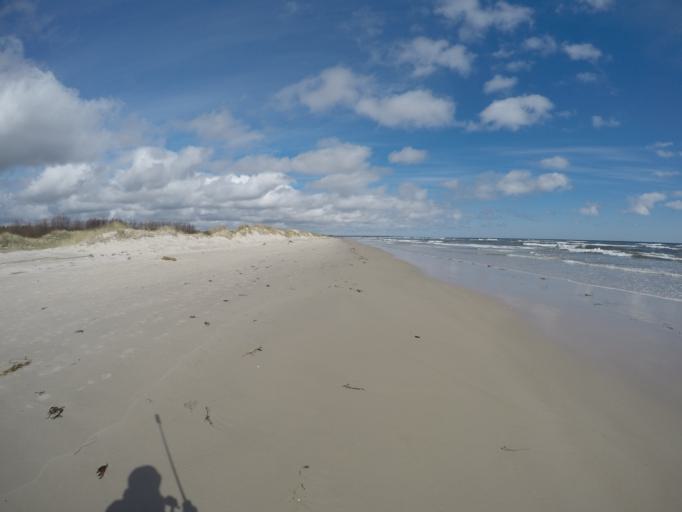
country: SE
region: Skane
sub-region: Simrishamns Kommun
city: Simrishamn
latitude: 55.4020
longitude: 14.2160
